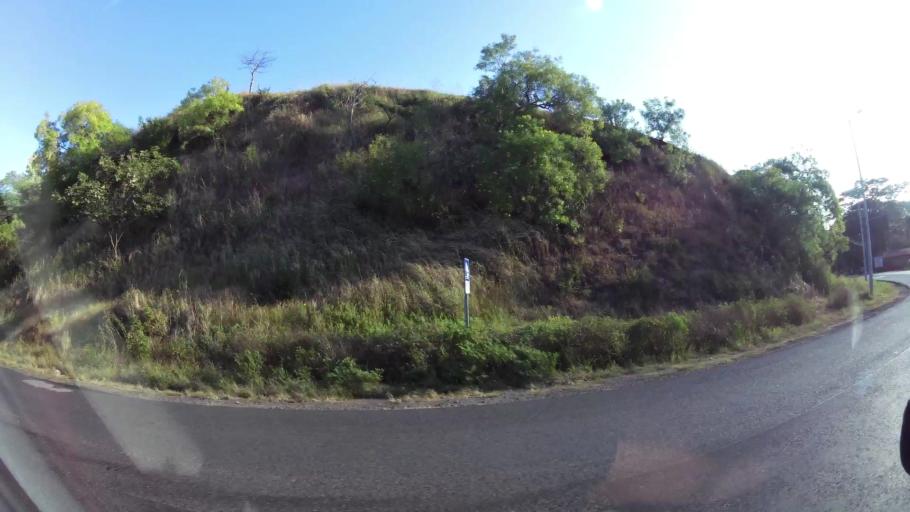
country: CR
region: Guanacaste
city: Sardinal
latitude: 10.5200
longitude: -85.6493
